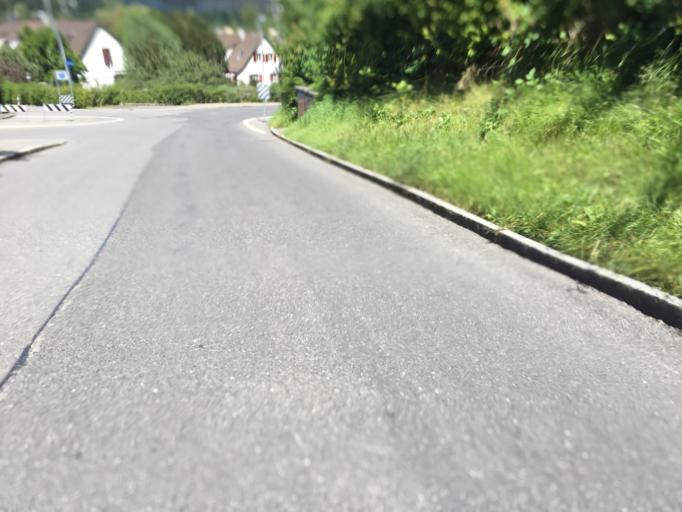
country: CH
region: Bern
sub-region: Bern-Mittelland District
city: Bern
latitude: 46.9669
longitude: 7.4503
